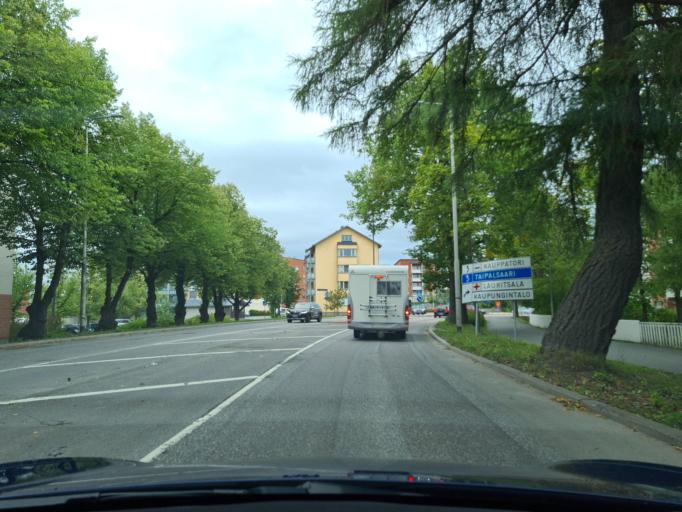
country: FI
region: South Karelia
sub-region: Lappeenranta
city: Lappeenranta
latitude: 61.0538
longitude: 28.1848
